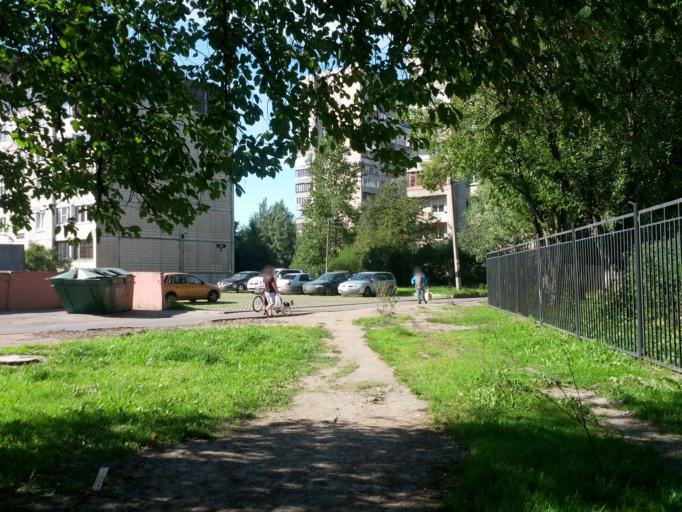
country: RU
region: Leningrad
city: Rybatskoye
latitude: 59.8944
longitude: 30.4880
